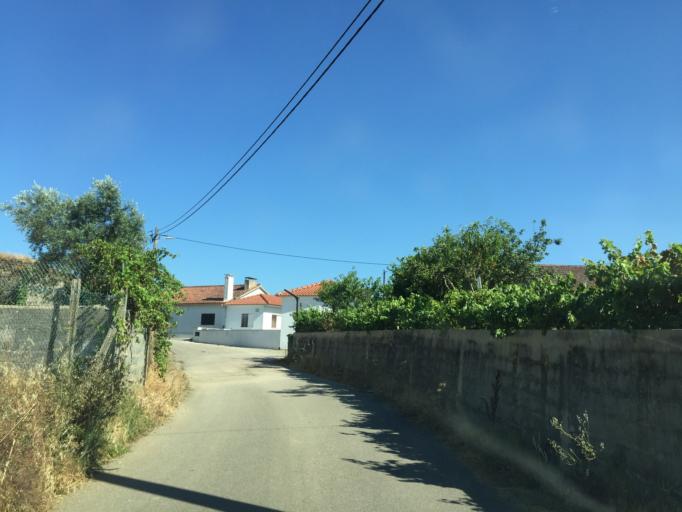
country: PT
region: Santarem
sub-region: Tomar
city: Tomar
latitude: 39.5968
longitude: -8.3241
